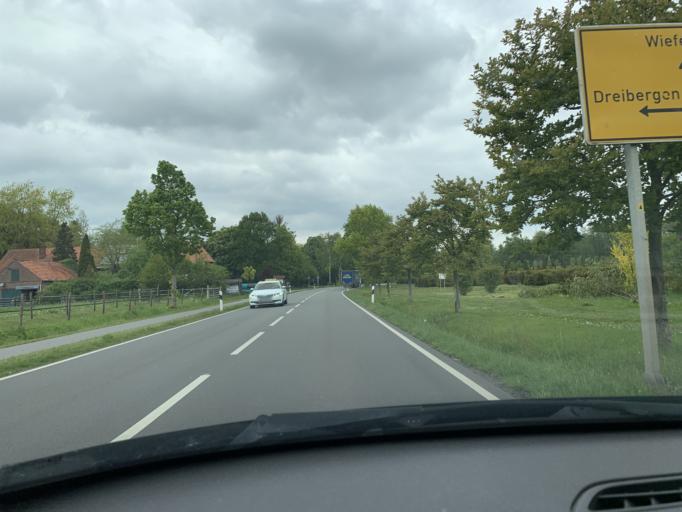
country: DE
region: Lower Saxony
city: Bad Zwischenahn
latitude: 53.2043
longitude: 8.0404
